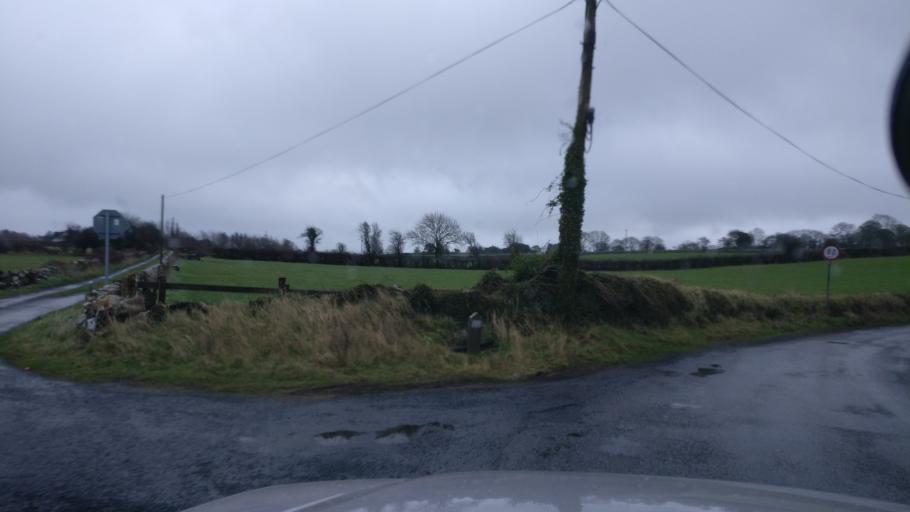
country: IE
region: Connaught
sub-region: County Galway
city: Loughrea
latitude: 53.1744
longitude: -8.6481
